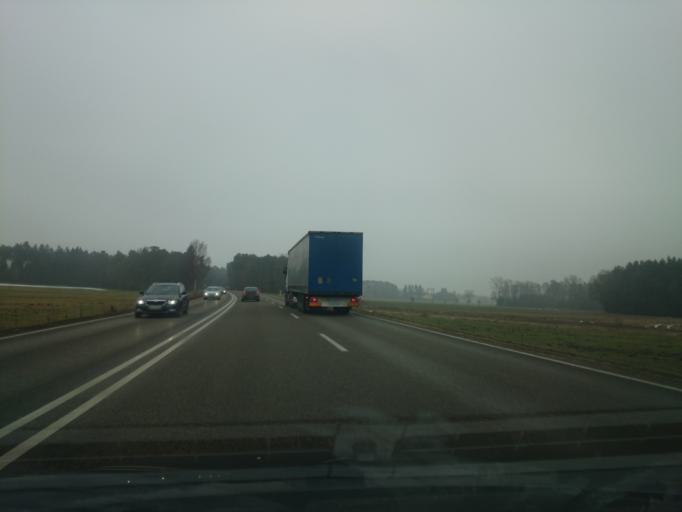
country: DE
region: Bavaria
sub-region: Upper Bavaria
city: Pornbach
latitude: 48.6219
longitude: 11.4415
